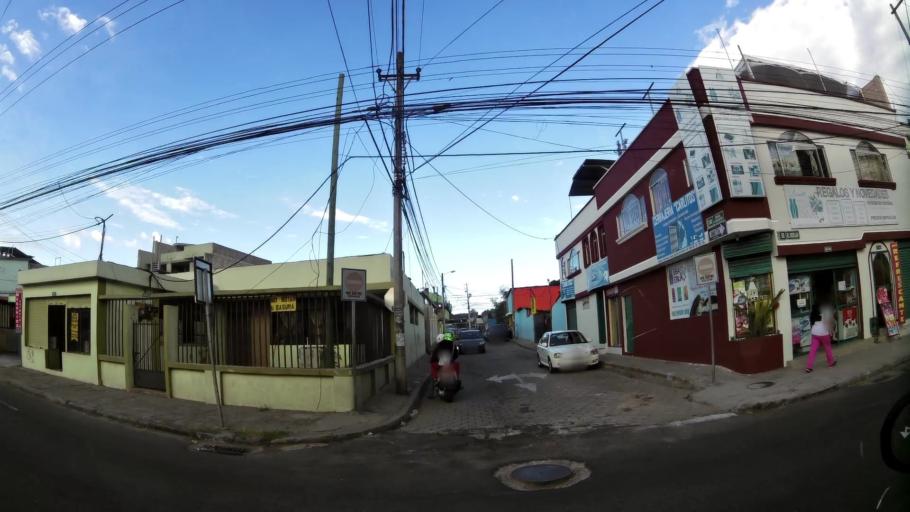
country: EC
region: Pichincha
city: Quito
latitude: -0.1497
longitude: -78.4765
